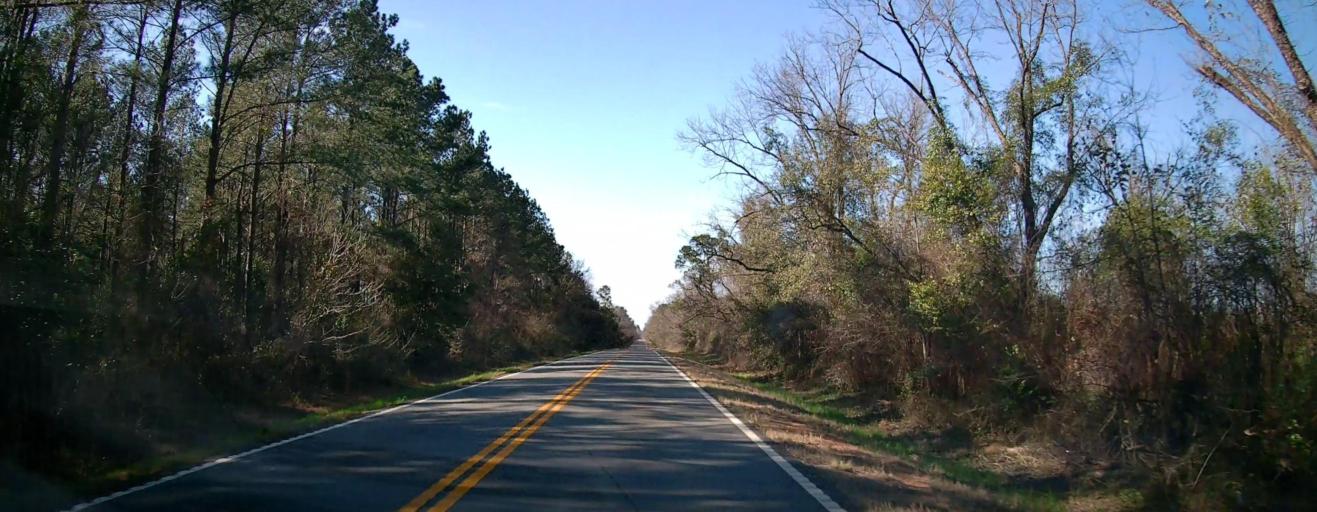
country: US
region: Georgia
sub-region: Macon County
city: Oglethorpe
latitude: 32.3866
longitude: -84.1946
